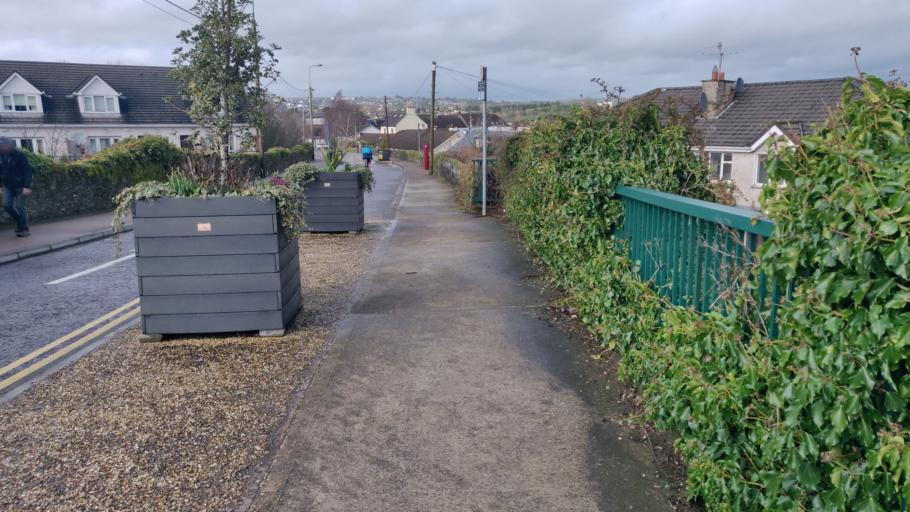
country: IE
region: Munster
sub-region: County Cork
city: Cork
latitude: 51.8742
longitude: -8.4345
